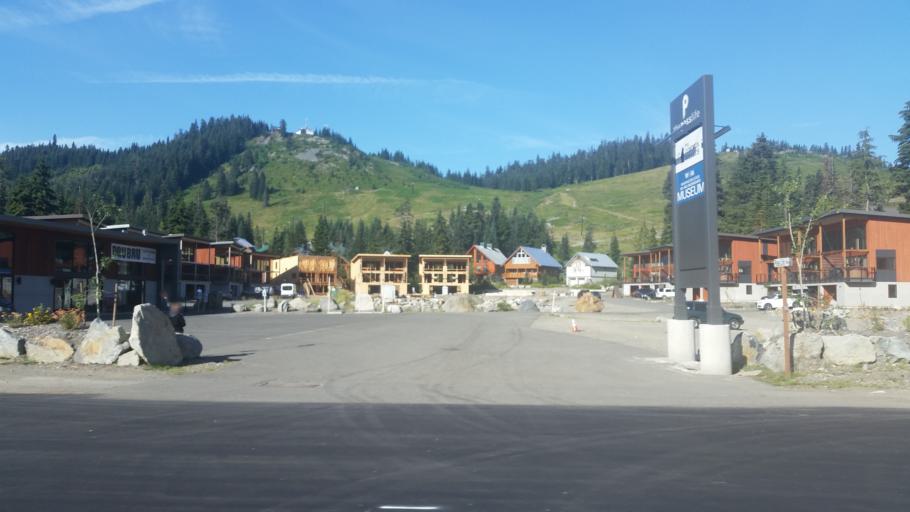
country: US
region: Washington
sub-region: King County
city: Tanner
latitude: 47.4217
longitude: -121.4121
